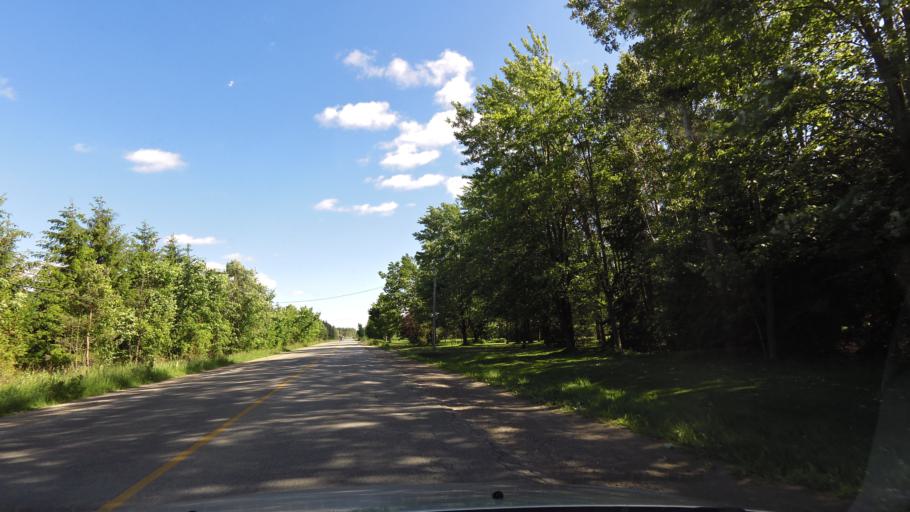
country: CA
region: Ontario
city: Bradford West Gwillimbury
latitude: 44.1475
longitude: -79.6122
